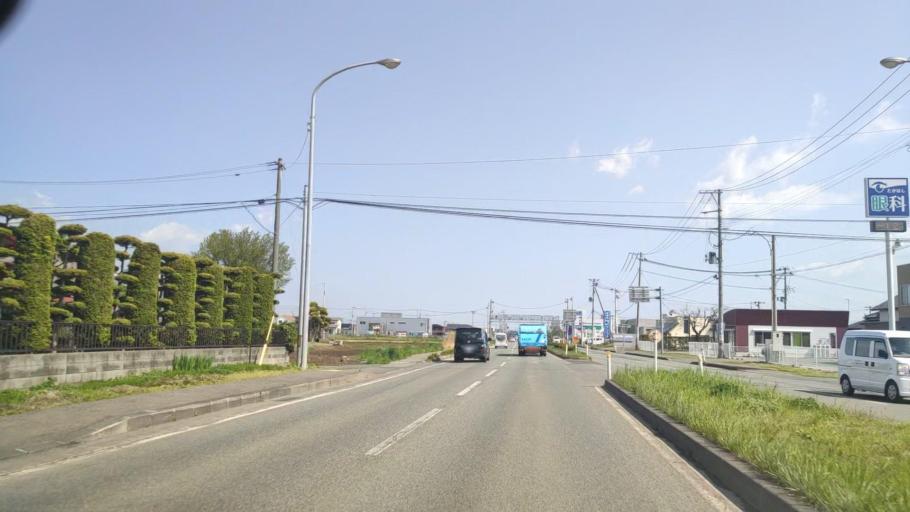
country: JP
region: Iwate
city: Morioka-shi
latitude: 39.6928
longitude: 141.1197
